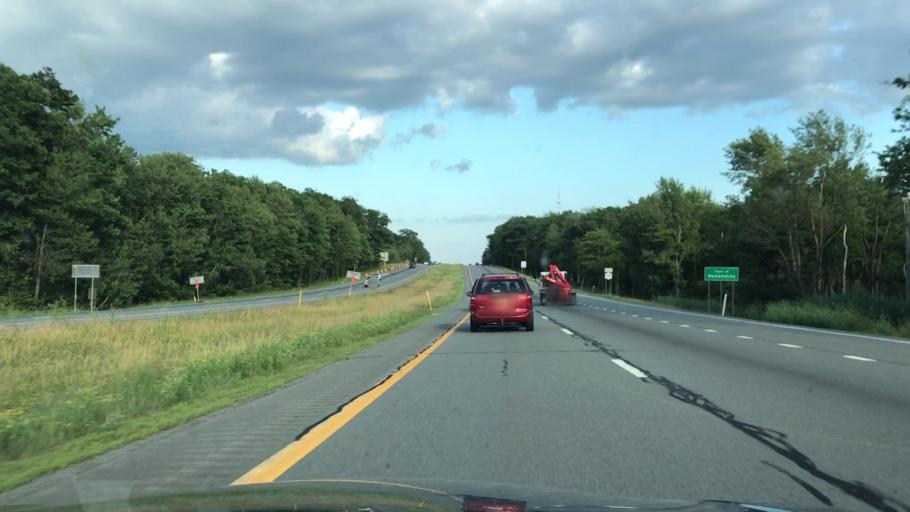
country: US
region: New York
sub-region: Sullivan County
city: Rock Hill
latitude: 41.6058
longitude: -74.5633
